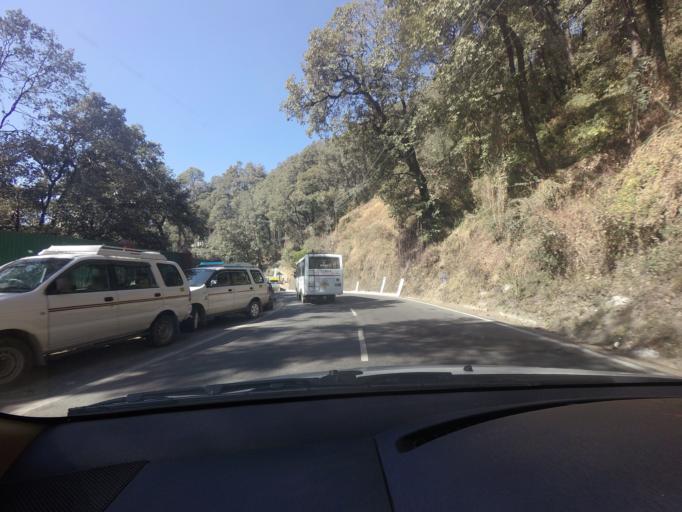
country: IN
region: Himachal Pradesh
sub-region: Shimla
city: Shimla
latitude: 31.1017
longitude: 77.1473
